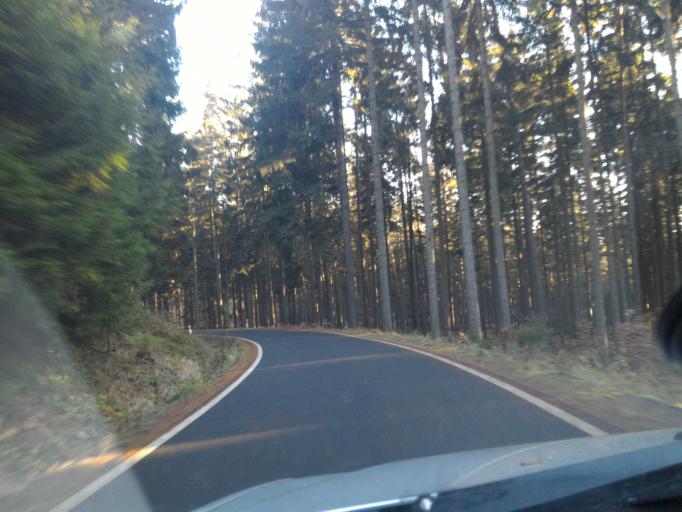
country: DE
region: Saxony
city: Kurort Oybin
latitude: 50.8125
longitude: 14.7140
